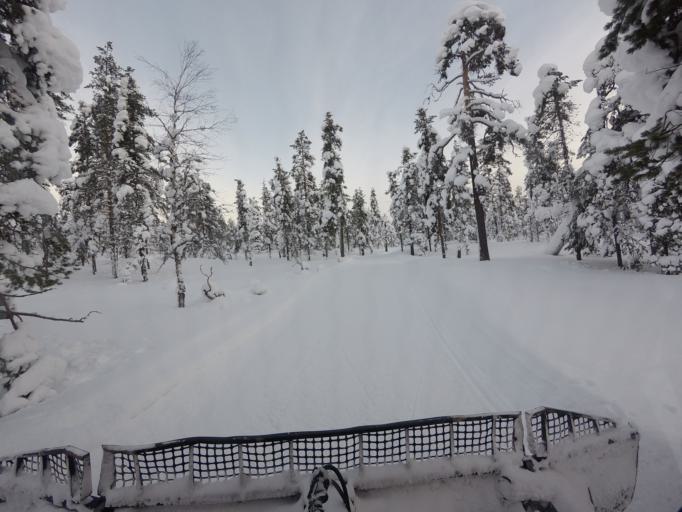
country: FI
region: Lapland
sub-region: Tunturi-Lappi
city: Kolari
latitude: 67.6543
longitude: 24.2482
